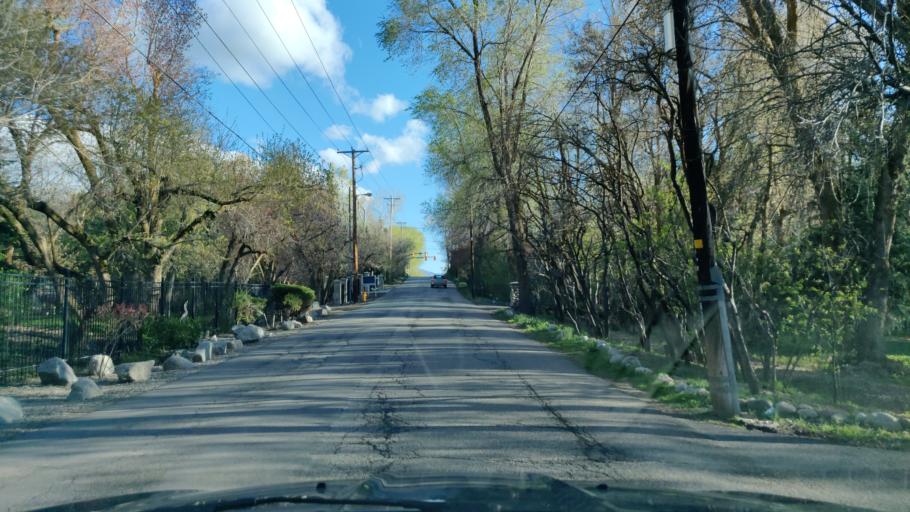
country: US
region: Utah
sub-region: Salt Lake County
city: Cottonwood Heights
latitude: 40.6403
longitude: -111.8248
